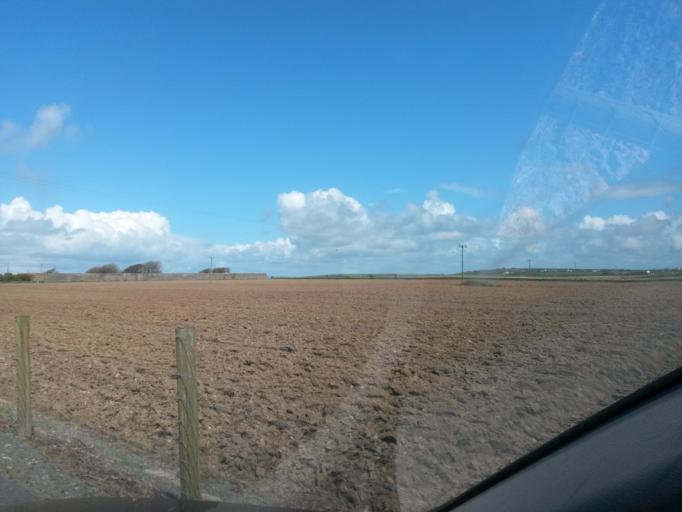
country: IE
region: Munster
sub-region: Waterford
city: Dunmore East
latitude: 52.1464
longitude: -6.9077
